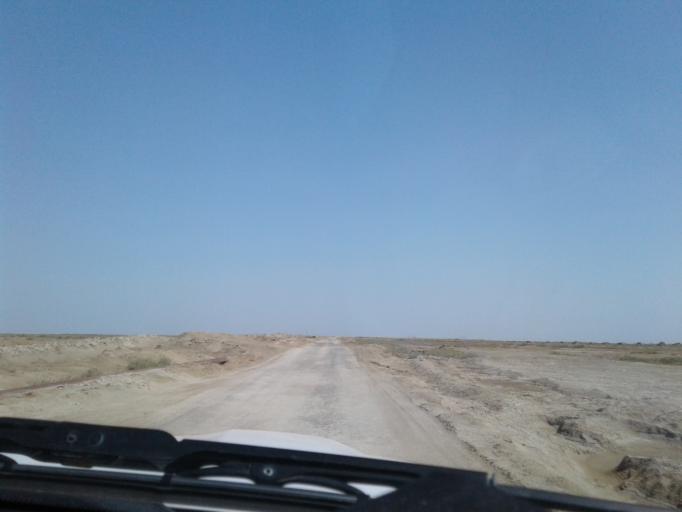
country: IR
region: Golestan
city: Gomishan
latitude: 37.8250
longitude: 53.9215
